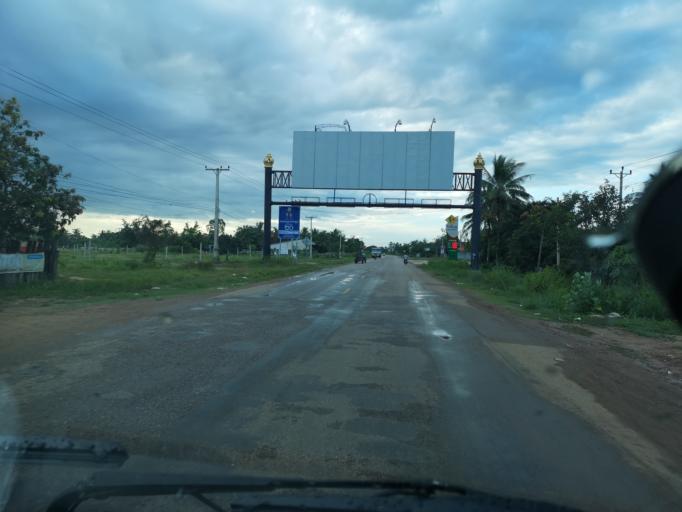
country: KH
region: Otar Meanchey
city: Samraong
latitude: 14.1655
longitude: 103.5175
